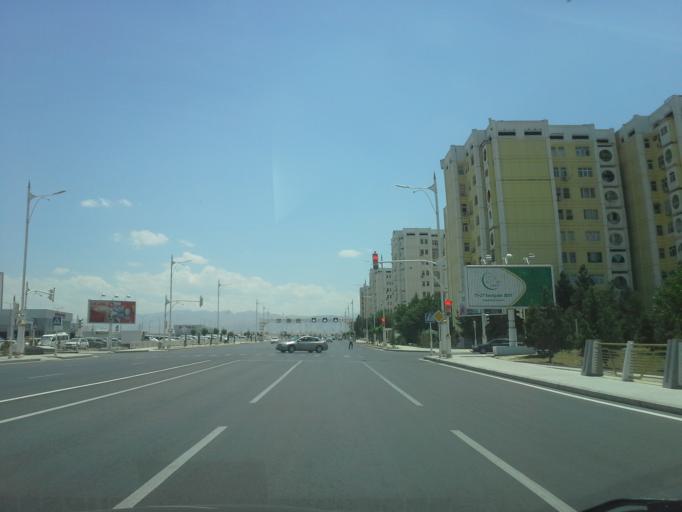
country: TM
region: Ahal
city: Ashgabat
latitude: 37.9066
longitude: 58.3977
